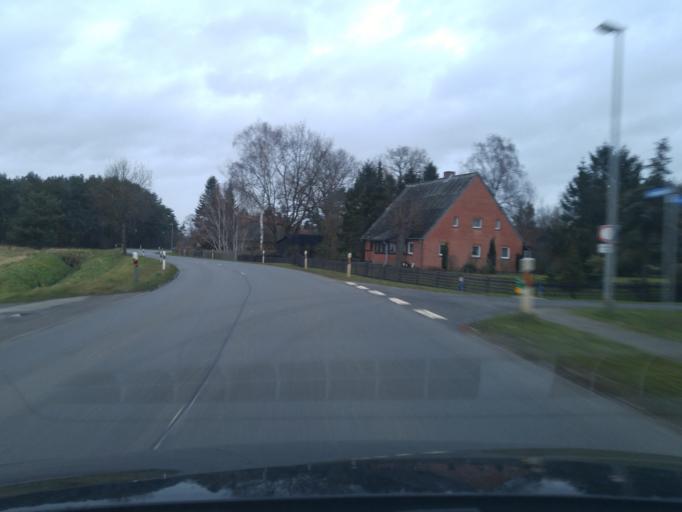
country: DE
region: Lower Saxony
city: Hittbergen
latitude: 53.3453
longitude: 10.5669
